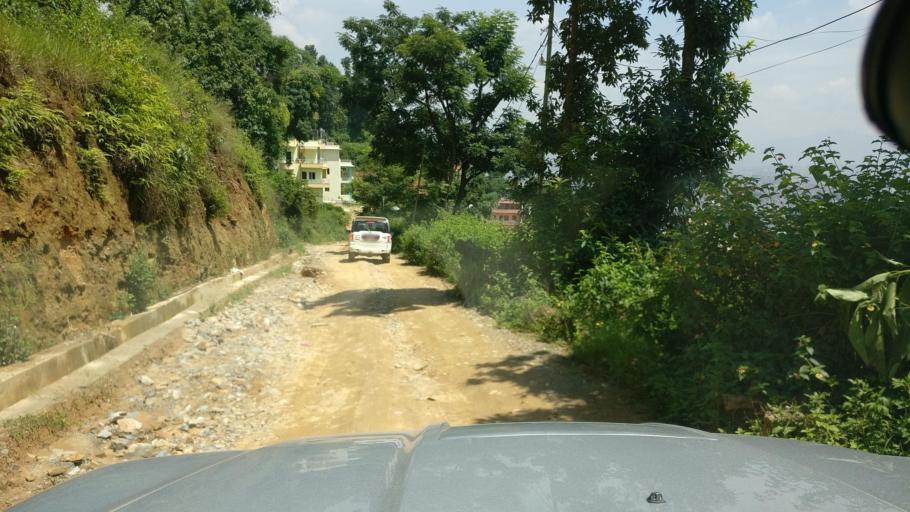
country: NP
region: Central Region
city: Kirtipur
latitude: 27.7028
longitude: 85.2561
